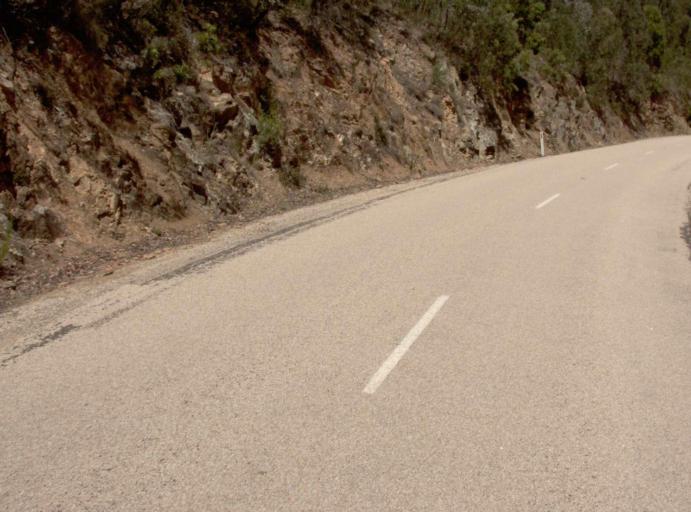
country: AU
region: Victoria
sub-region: East Gippsland
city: Bairnsdale
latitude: -37.4571
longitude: 147.8311
